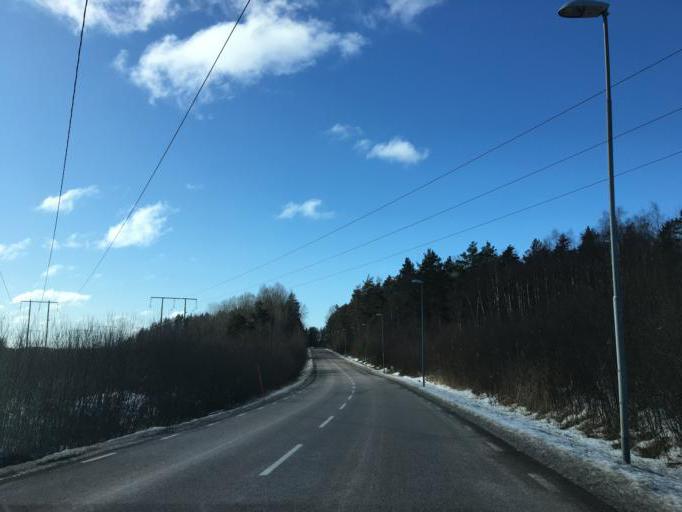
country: SE
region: Vaestmanland
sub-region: Vasteras
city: Vasteras
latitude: 59.6071
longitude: 16.4623
